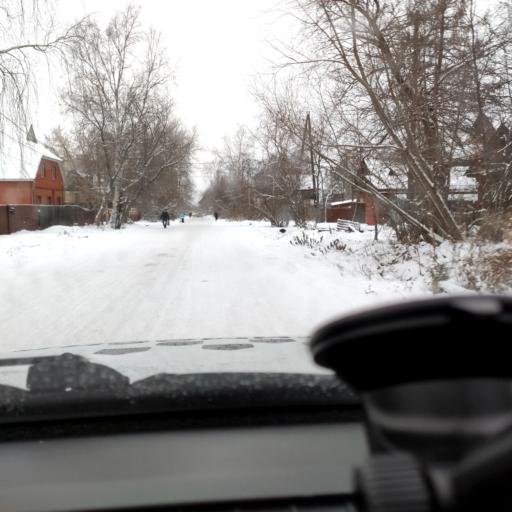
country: RU
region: Perm
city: Perm
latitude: 58.0610
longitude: 56.3653
